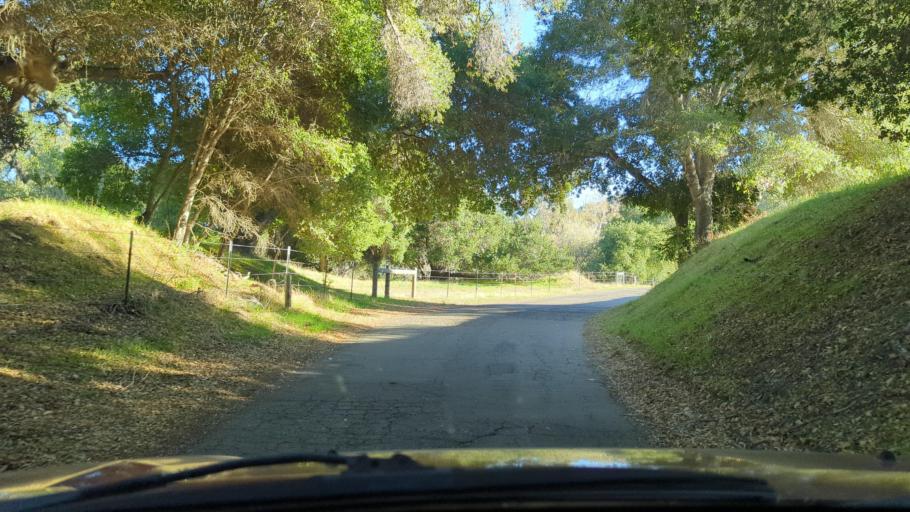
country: US
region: California
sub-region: Santa Barbara County
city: Santa Ynez
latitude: 34.5635
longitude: -120.0908
